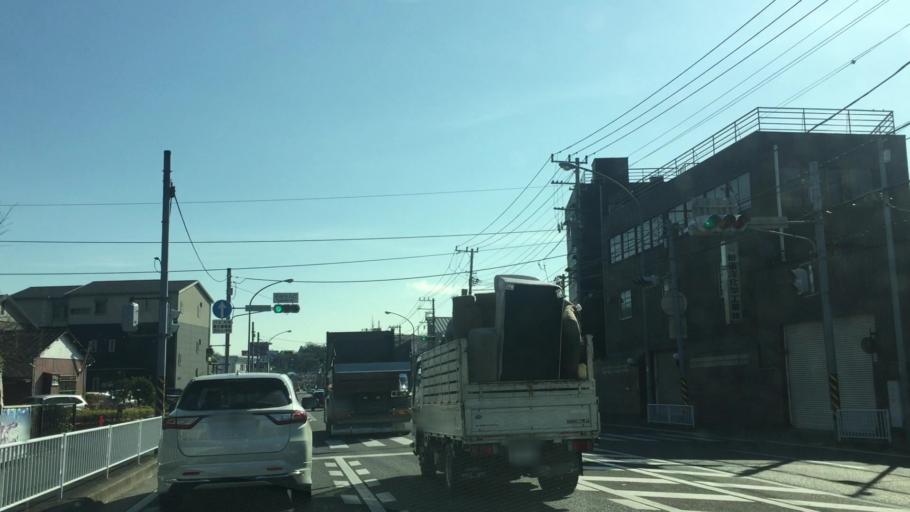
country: JP
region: Kanagawa
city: Yokohama
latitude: 35.3736
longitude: 139.6112
